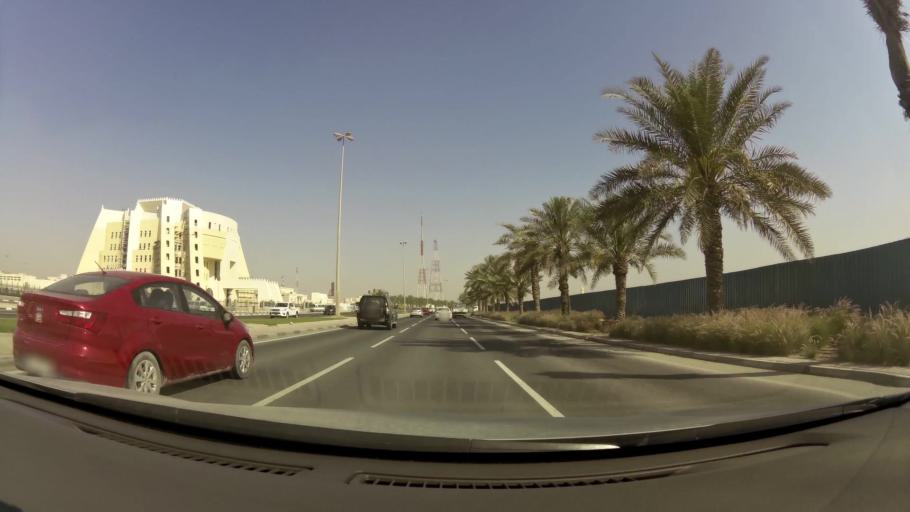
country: QA
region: Baladiyat ad Dawhah
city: Doha
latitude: 25.3065
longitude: 51.5056
